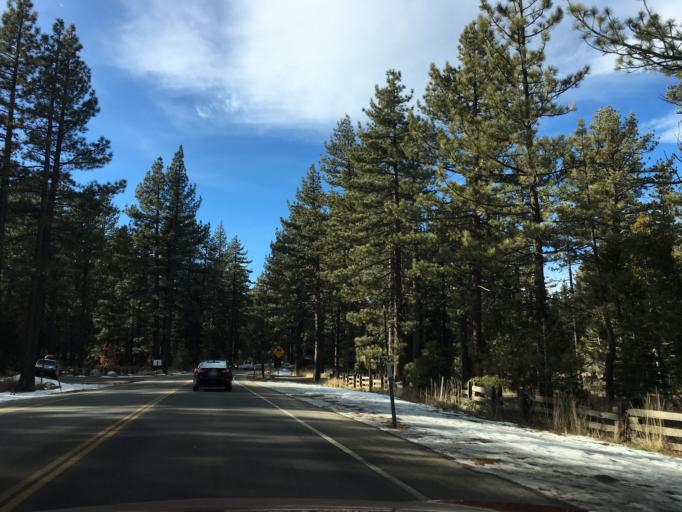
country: US
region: California
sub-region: El Dorado County
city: South Lake Tahoe
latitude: 38.9332
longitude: -120.0367
